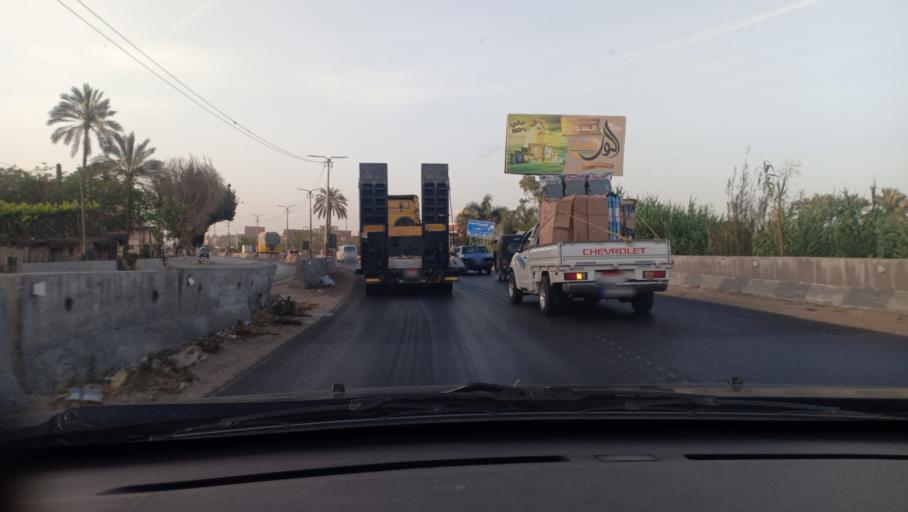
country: EG
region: Muhafazat al Minufiyah
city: Quwaysina
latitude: 30.5410
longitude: 31.2692
